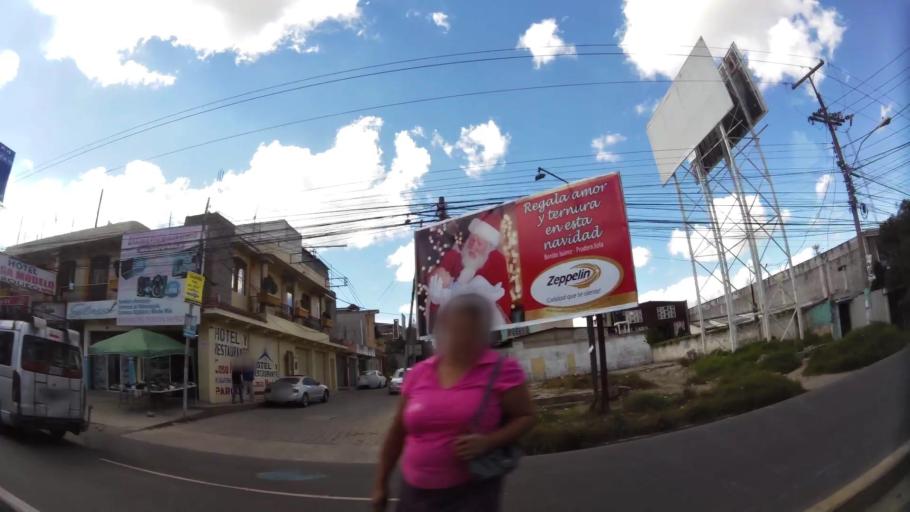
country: GT
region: Quetzaltenango
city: Quetzaltenango
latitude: 14.8495
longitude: -91.5369
